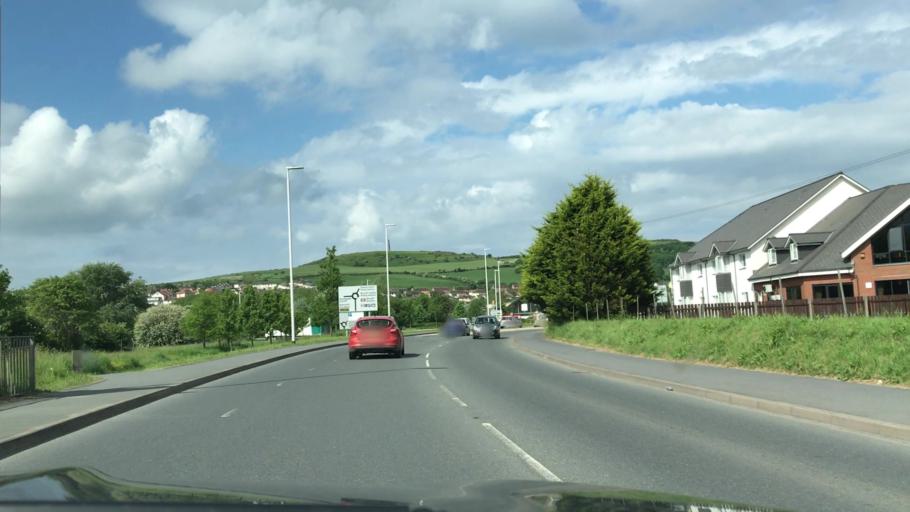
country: GB
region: Wales
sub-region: County of Ceredigion
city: Penparcau
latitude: 52.4047
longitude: -4.0635
